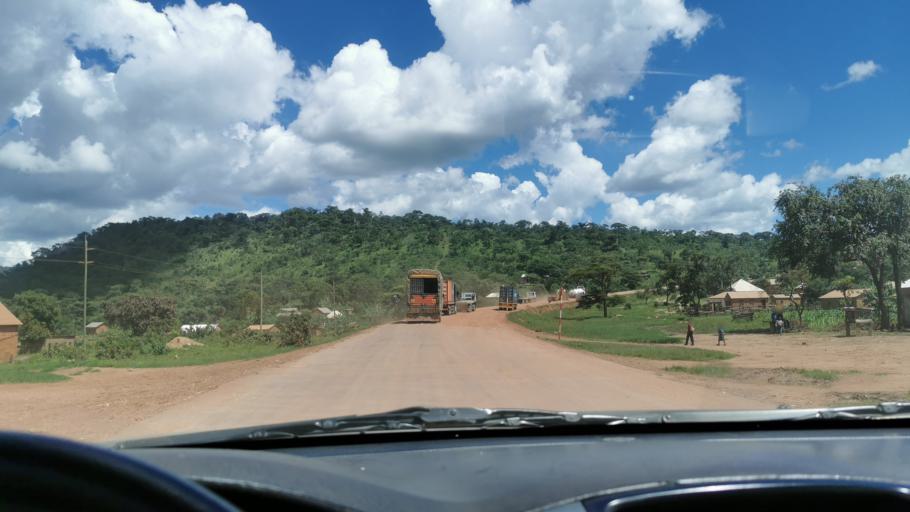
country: TZ
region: Kagera
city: Biharamulo
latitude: -2.8899
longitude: 31.1574
